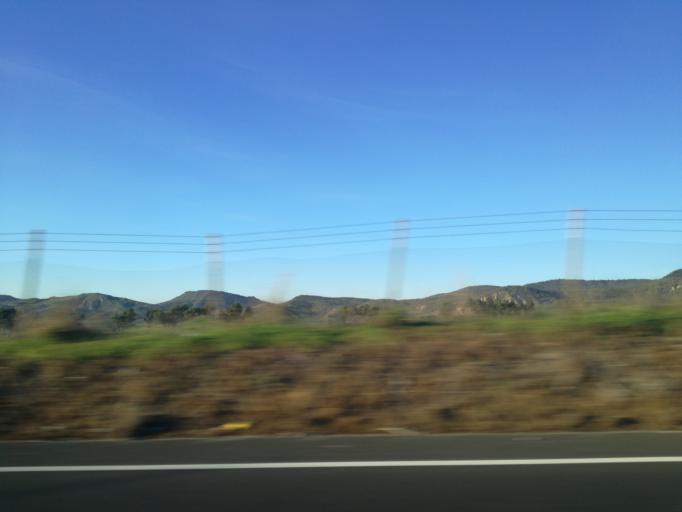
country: IT
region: Sicily
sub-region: Catania
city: San Michele di Ganzaria
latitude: 37.2146
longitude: 14.4092
